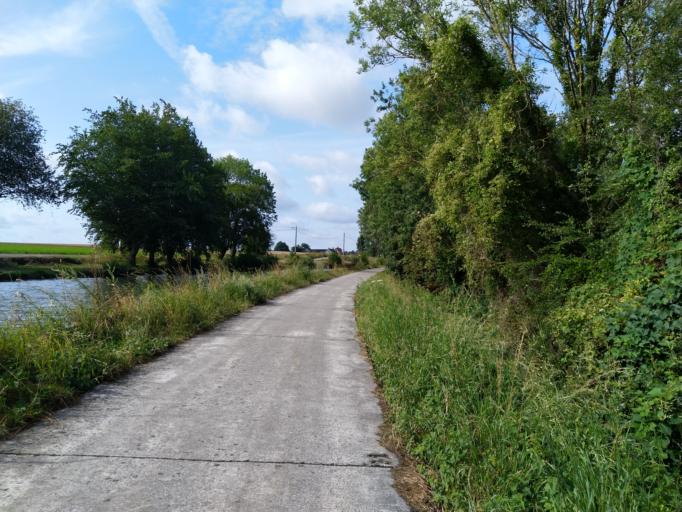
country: BE
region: Wallonia
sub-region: Province du Hainaut
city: Chievres
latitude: 50.5829
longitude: 3.7796
